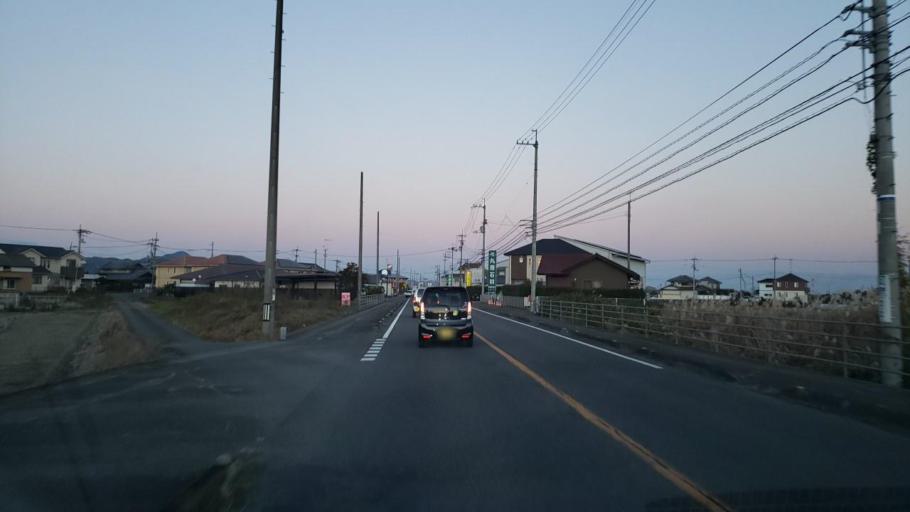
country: JP
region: Tokushima
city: Ishii
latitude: 34.1137
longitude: 134.4184
